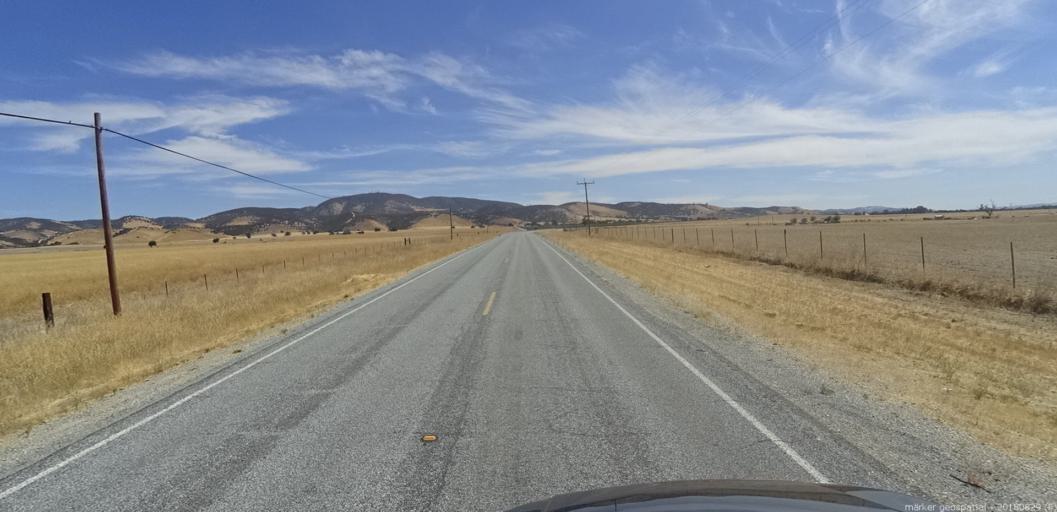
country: US
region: California
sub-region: San Luis Obispo County
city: Lake Nacimiento
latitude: 35.9368
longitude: -121.0684
